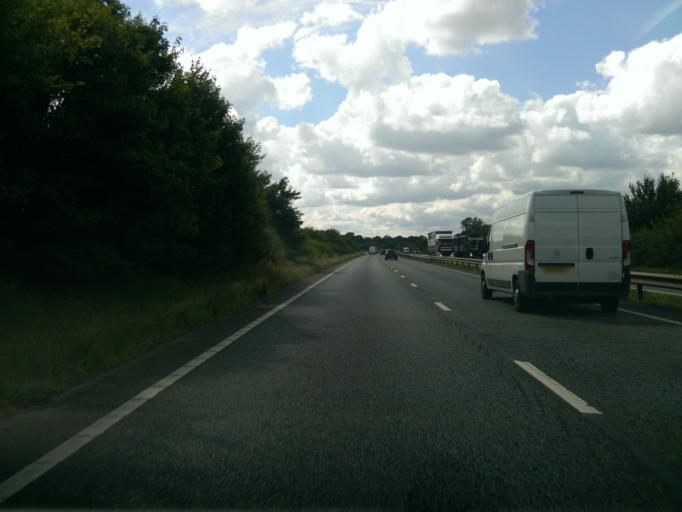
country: GB
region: England
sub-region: Northamptonshire
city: Desborough
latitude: 52.4051
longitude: -0.8784
